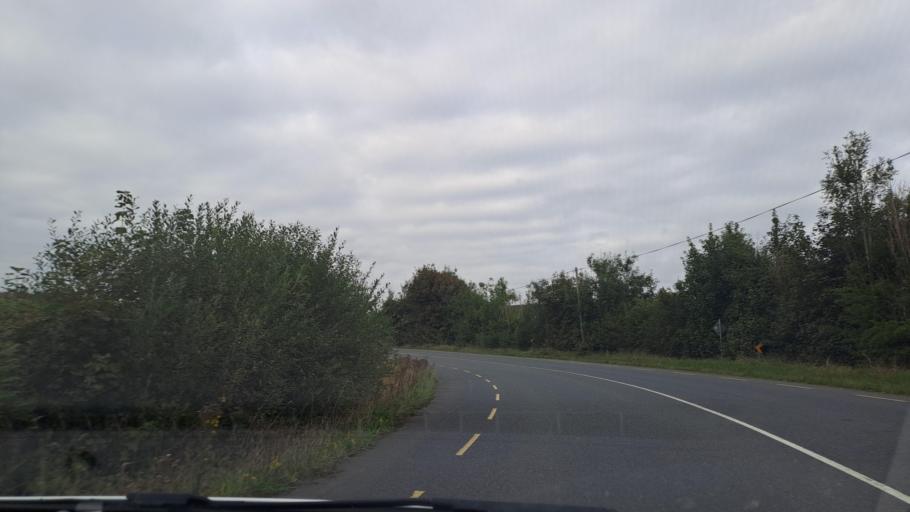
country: IE
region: Ulster
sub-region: County Monaghan
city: Carrickmacross
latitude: 54.0287
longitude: -6.7757
